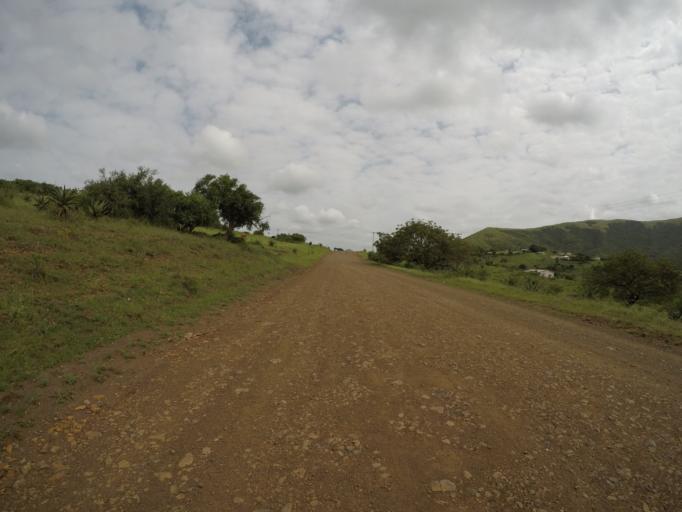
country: ZA
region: KwaZulu-Natal
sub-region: uThungulu District Municipality
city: Empangeni
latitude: -28.6155
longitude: 31.9004
